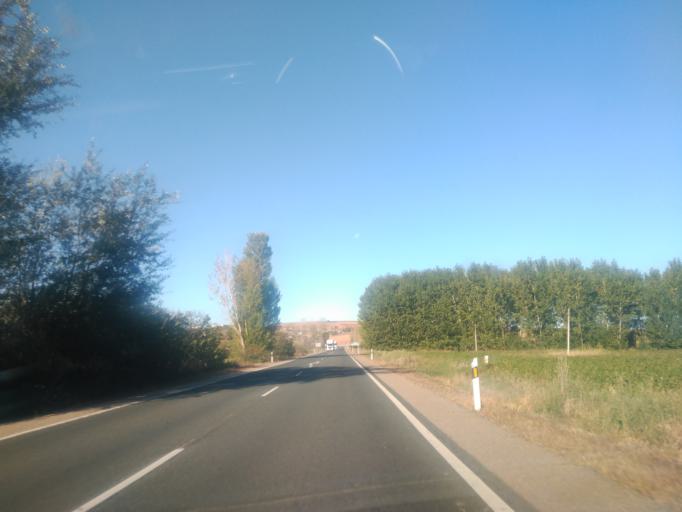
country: ES
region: Castille and Leon
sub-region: Provincia de Burgos
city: Fuentecen
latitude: 41.6308
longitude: -3.8536
